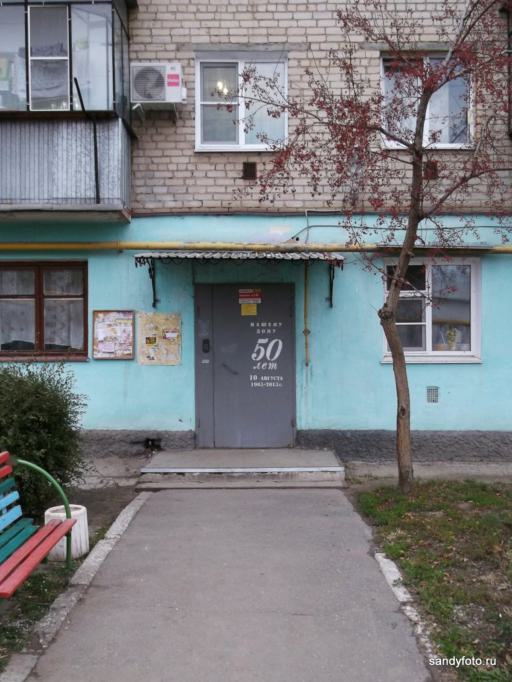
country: RU
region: Chelyabinsk
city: Troitsk
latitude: 54.0896
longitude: 61.5686
